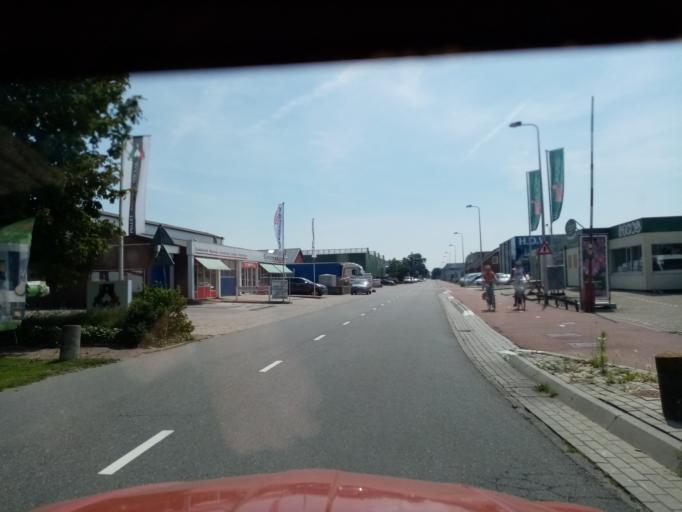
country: NL
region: South Holland
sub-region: Gemeente Kaag en Braassem
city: Leimuiden
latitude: 52.1799
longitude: 4.7115
